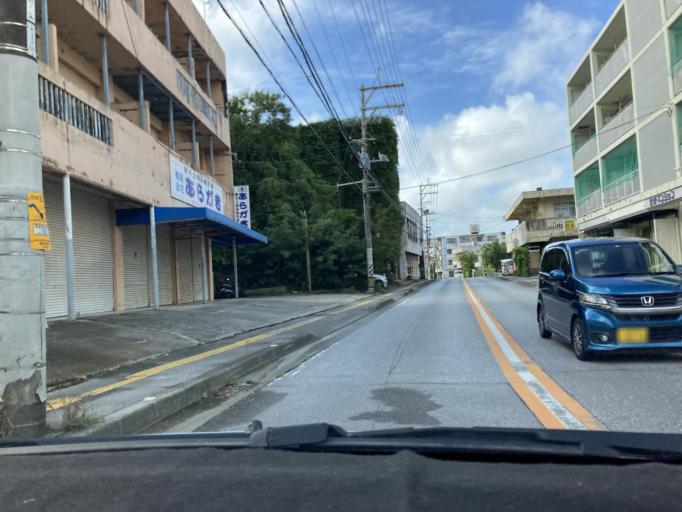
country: JP
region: Okinawa
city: Tomigusuku
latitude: 26.1806
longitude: 127.6852
